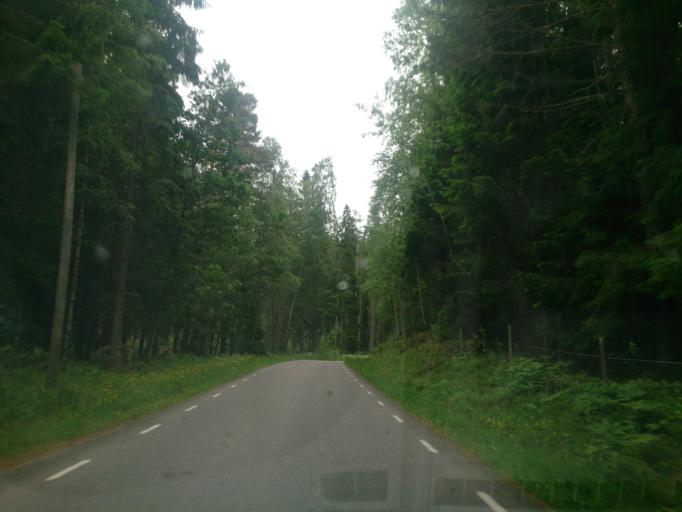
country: SE
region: OEstergoetland
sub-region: Atvidabergs Kommun
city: Atvidaberg
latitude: 58.2906
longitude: 16.0955
